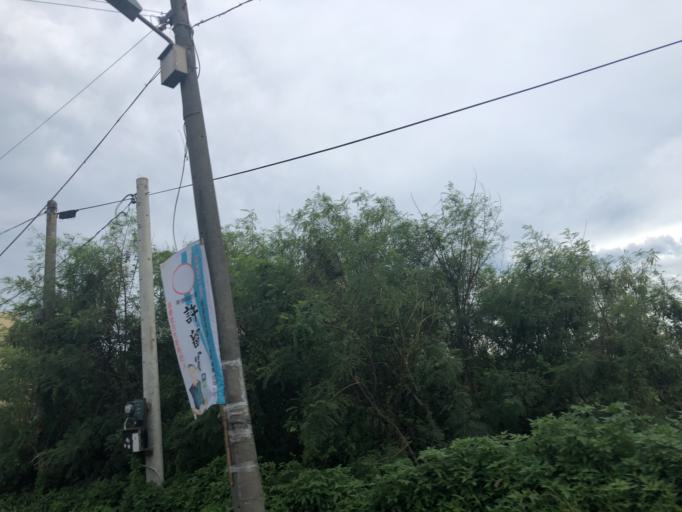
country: TW
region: Taiwan
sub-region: Chiayi
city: Taibao
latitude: 23.7070
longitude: 120.2005
